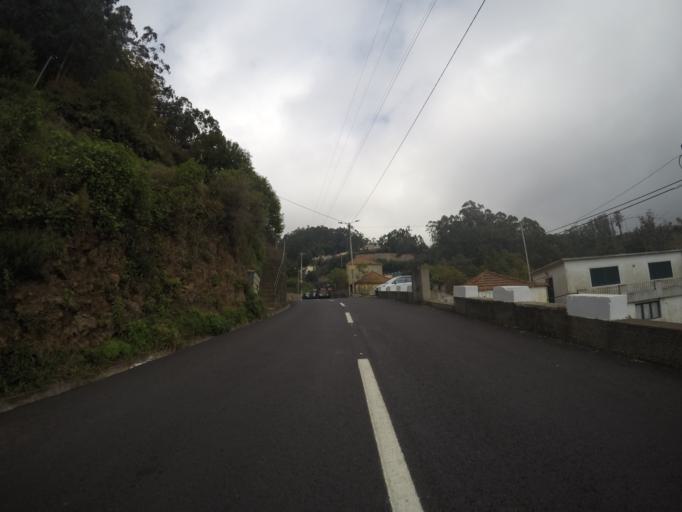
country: PT
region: Madeira
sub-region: Camara de Lobos
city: Curral das Freiras
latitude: 32.6869
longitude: -16.9533
